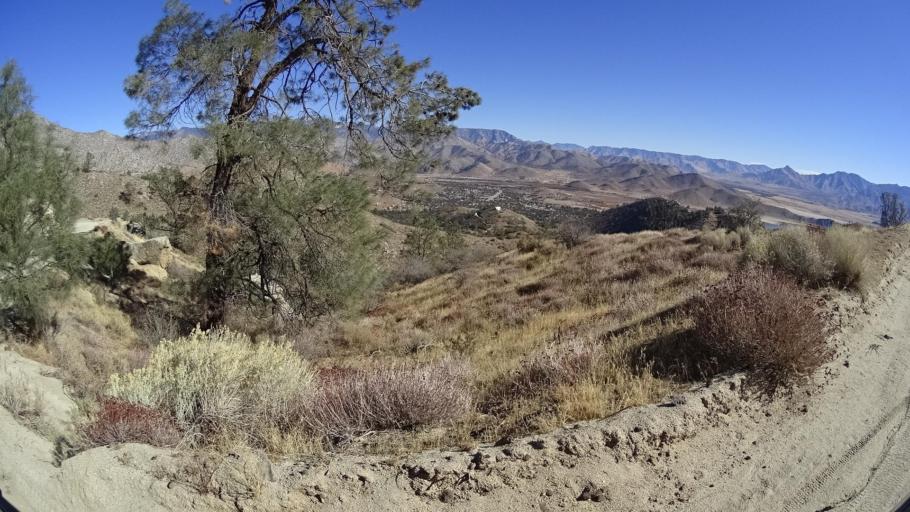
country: US
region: California
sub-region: Kern County
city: Wofford Heights
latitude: 35.7023
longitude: -118.4899
